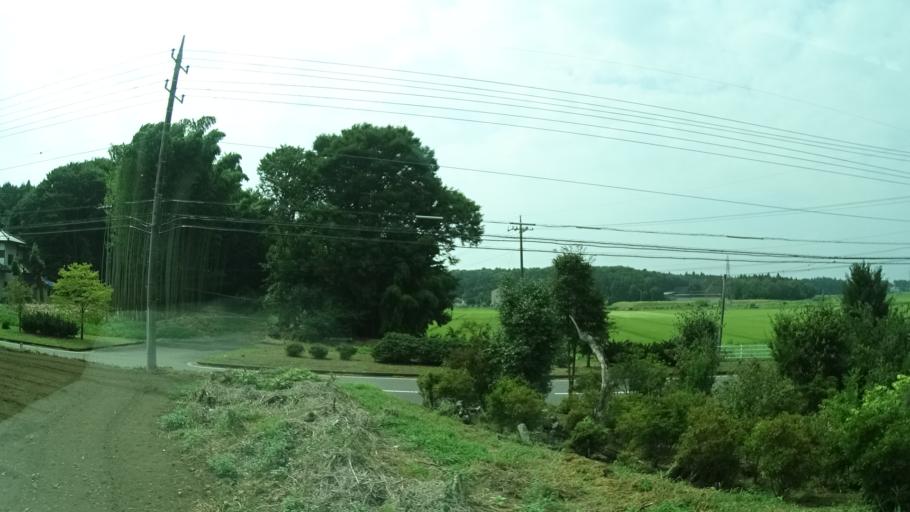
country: JP
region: Tochigi
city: Mashiko
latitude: 36.5196
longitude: 140.0903
